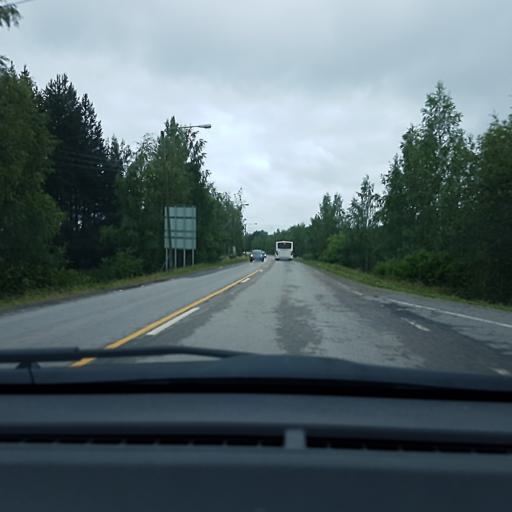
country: FI
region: Uusimaa
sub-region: Helsinki
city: Sibbo
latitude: 60.3683
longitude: 25.2304
